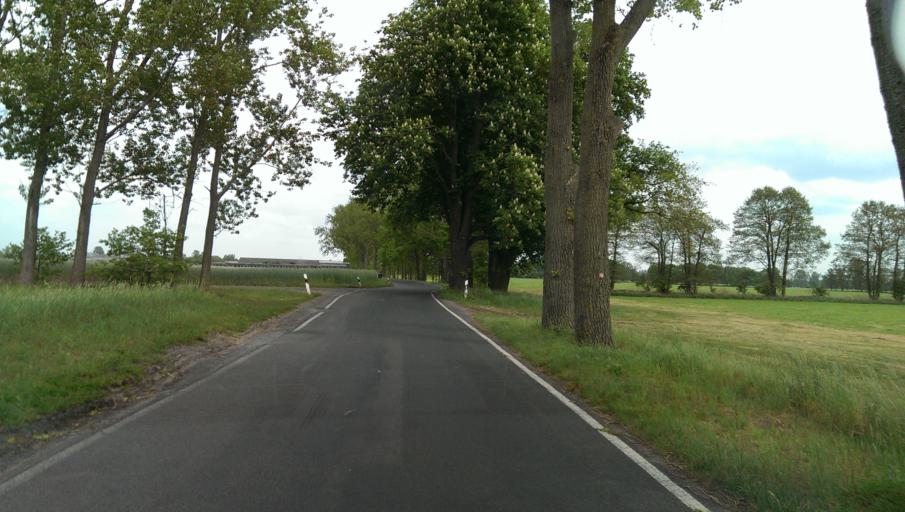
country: DE
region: Brandenburg
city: Linthe
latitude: 52.1503
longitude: 12.8297
